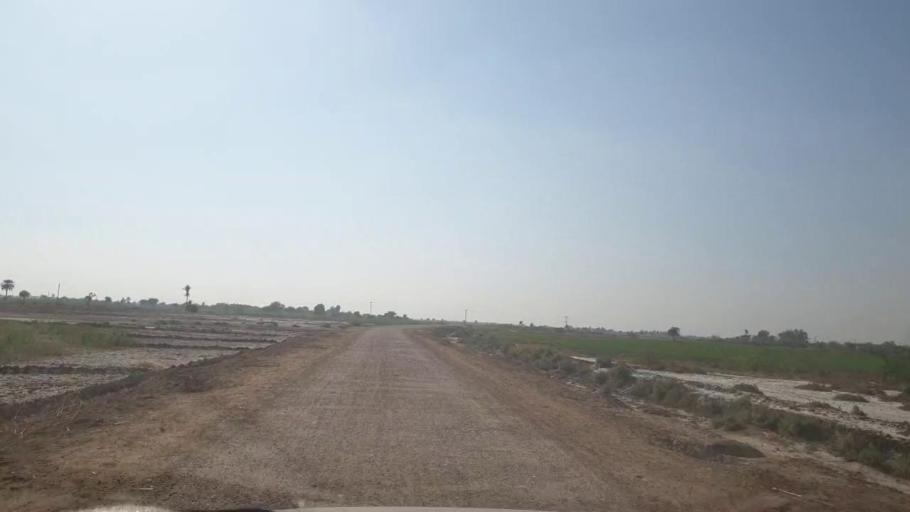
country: PK
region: Sindh
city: Mirpur Khas
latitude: 25.4557
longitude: 69.1250
